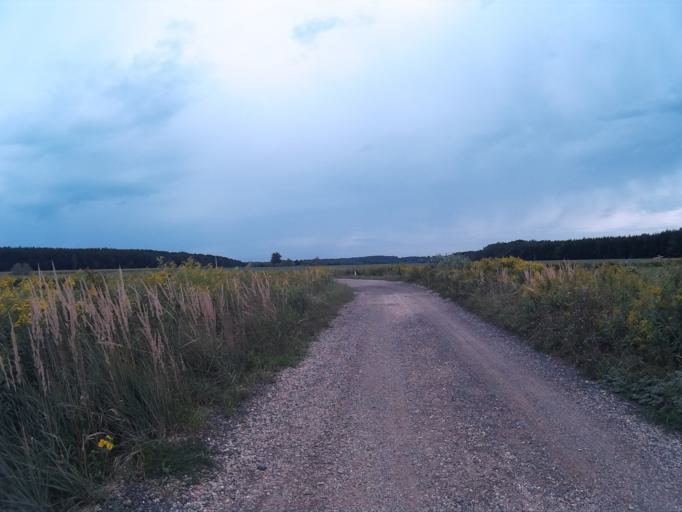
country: SI
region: Kobilje
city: Kobilje
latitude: 46.7420
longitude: 16.4460
